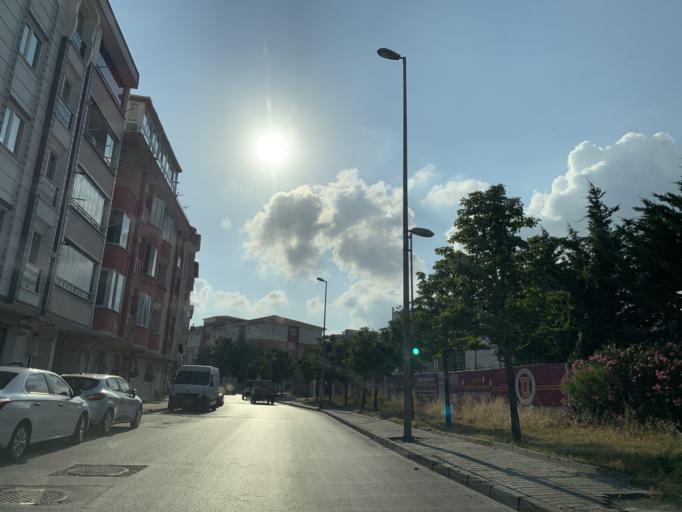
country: TR
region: Istanbul
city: Esenyurt
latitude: 41.0462
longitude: 28.6809
